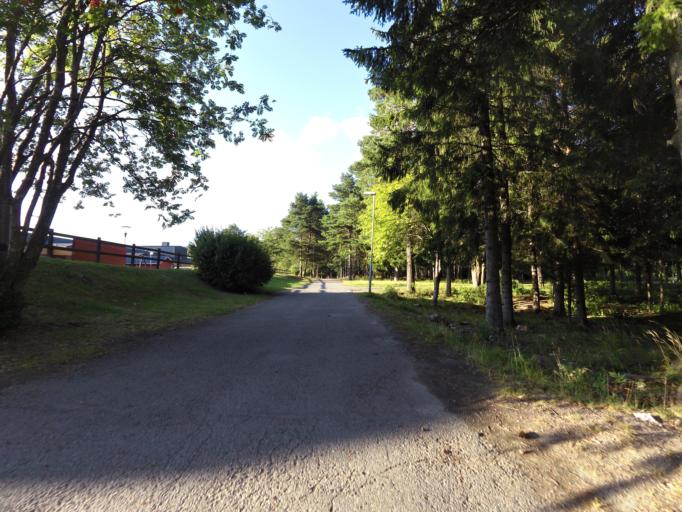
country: SE
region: Gaevleborg
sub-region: Gavle Kommun
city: Gavle
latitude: 60.6513
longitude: 17.1407
